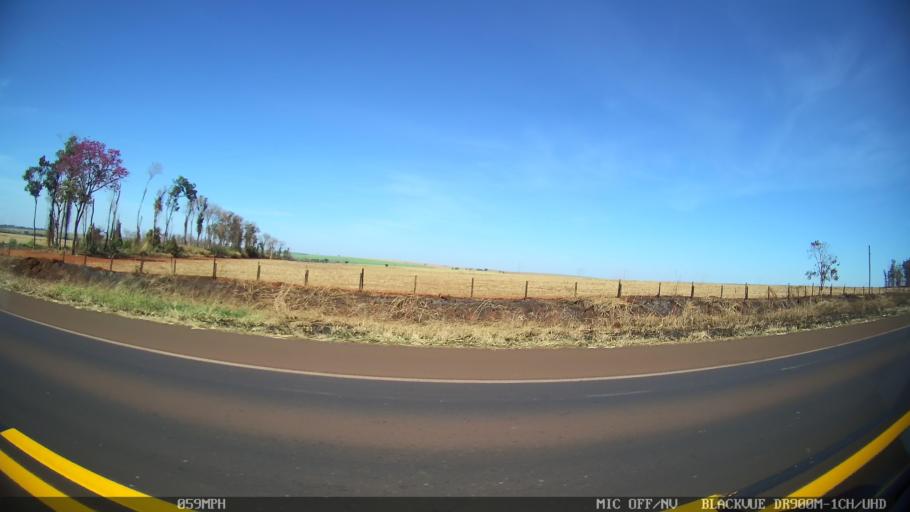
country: BR
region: Sao Paulo
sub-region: Barretos
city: Barretos
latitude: -20.4884
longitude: -48.5175
